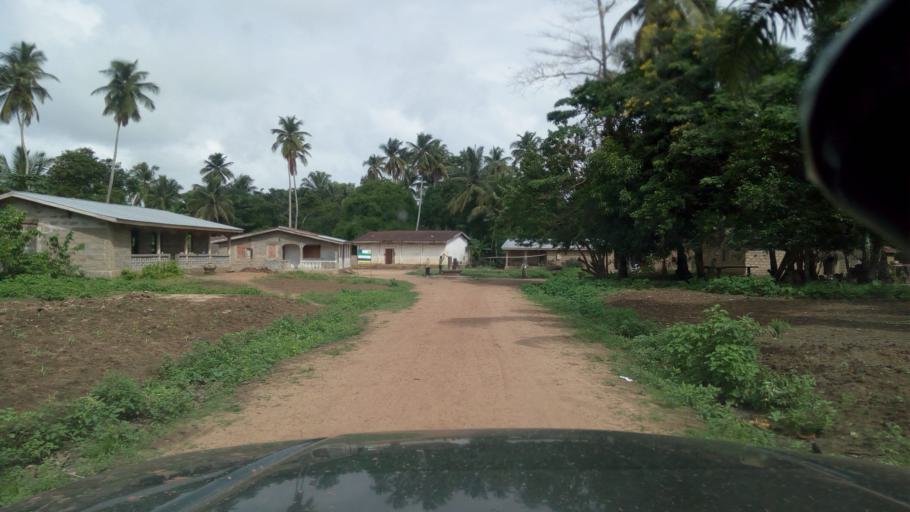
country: SL
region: Northern Province
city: Mambolo
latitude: 8.8321
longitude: -12.9583
